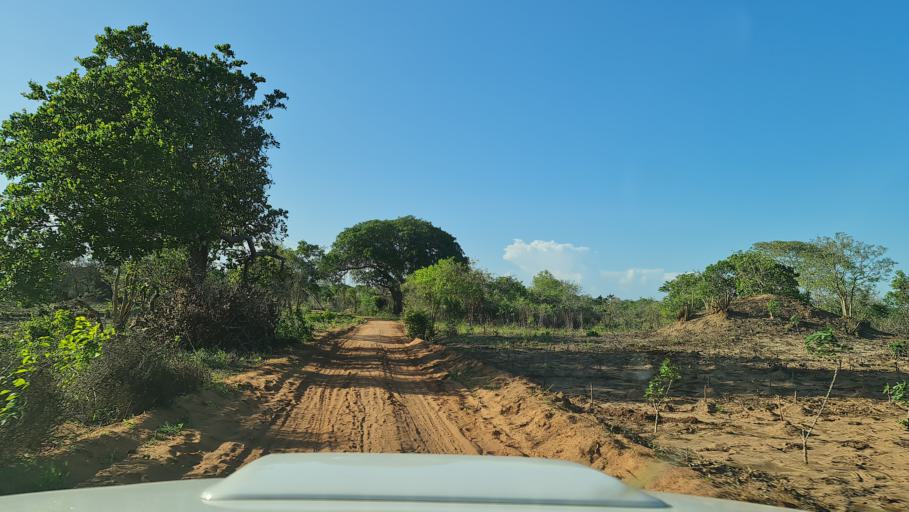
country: MZ
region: Nampula
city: Nacala
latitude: -14.7027
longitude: 40.3300
